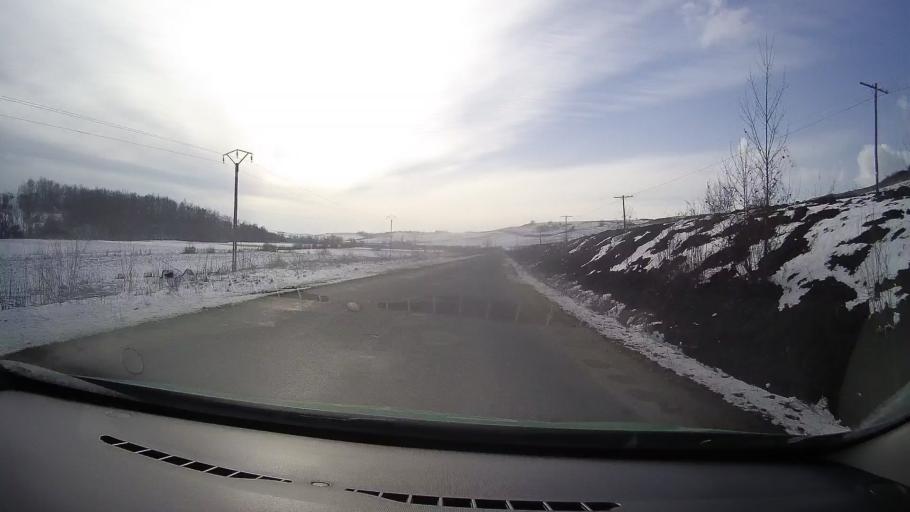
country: RO
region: Sibiu
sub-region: Comuna Iacobeni
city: Iacobeni
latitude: 46.0162
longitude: 24.6944
